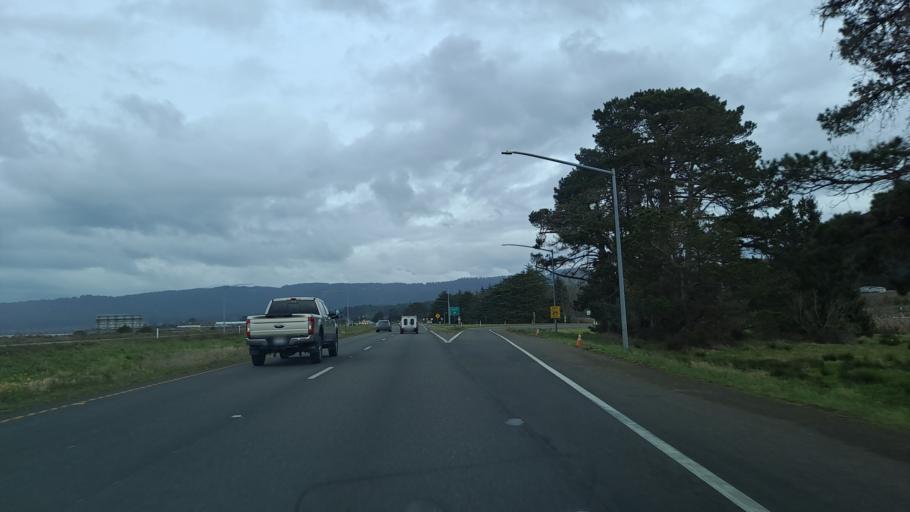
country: US
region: California
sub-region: Humboldt County
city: Bayside
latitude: 40.8194
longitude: -124.0950
